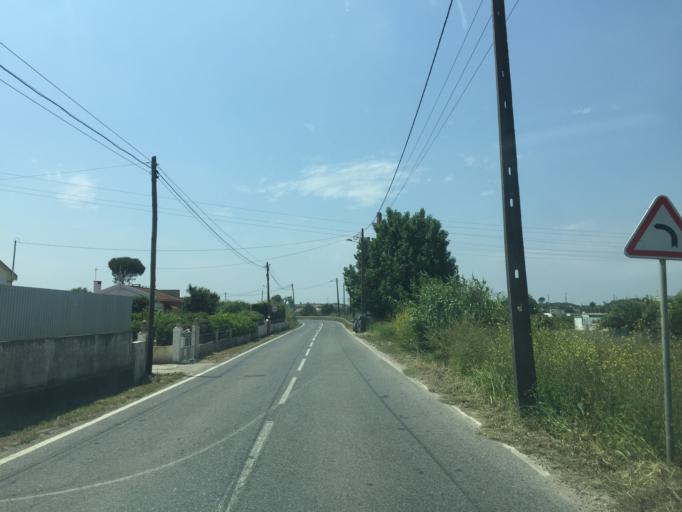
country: PT
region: Lisbon
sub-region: Mafra
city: Venda do Pinheiro
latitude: 38.8915
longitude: -9.1887
